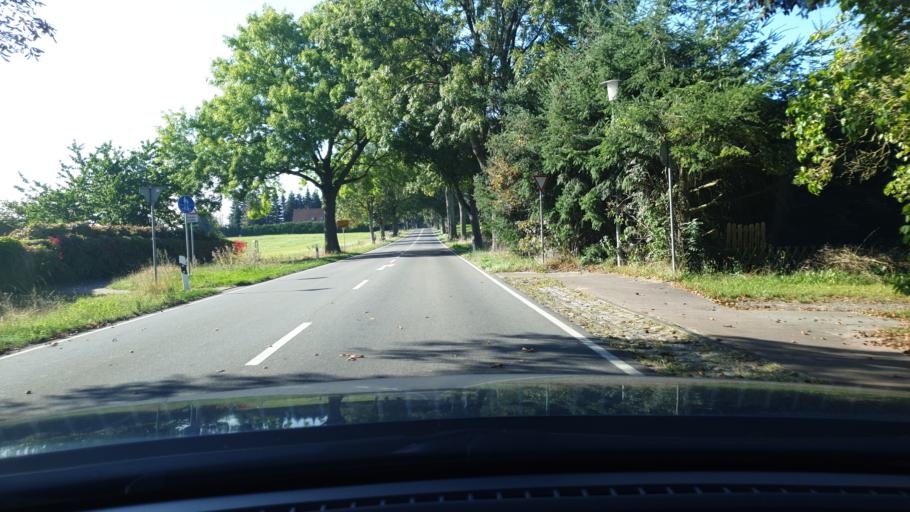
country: DE
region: Mecklenburg-Vorpommern
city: Lutzow
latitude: 53.6469
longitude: 11.1688
